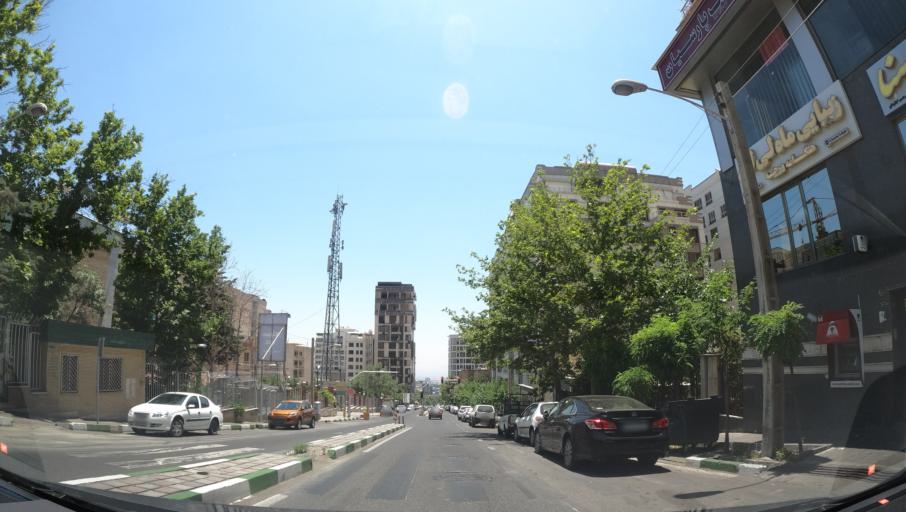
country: IR
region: Tehran
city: Tajrish
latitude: 35.8082
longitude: 51.4010
